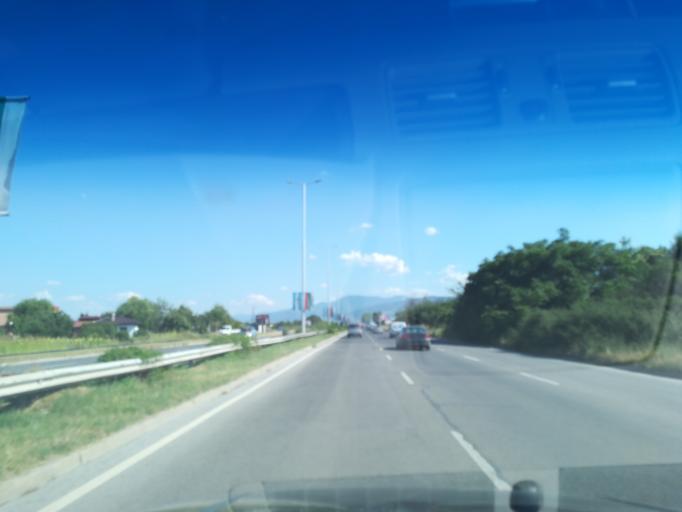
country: BG
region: Plovdiv
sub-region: Obshtina Plovdiv
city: Plovdiv
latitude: 42.1054
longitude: 24.7841
